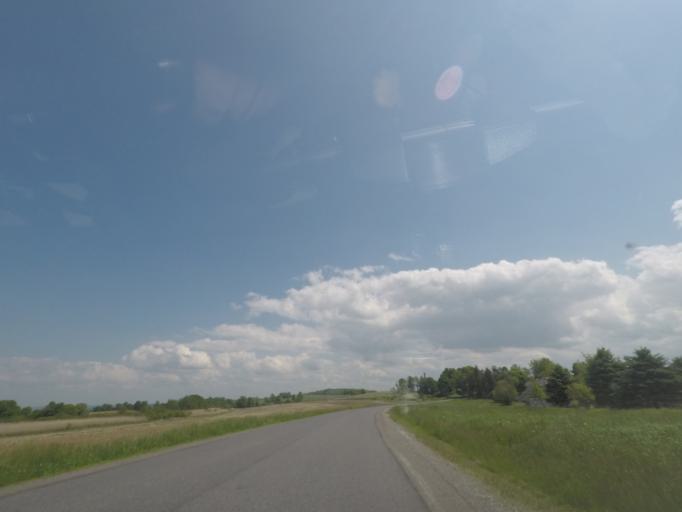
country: US
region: New York
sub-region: Dutchess County
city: Pine Plains
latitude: 41.9747
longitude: -73.5477
